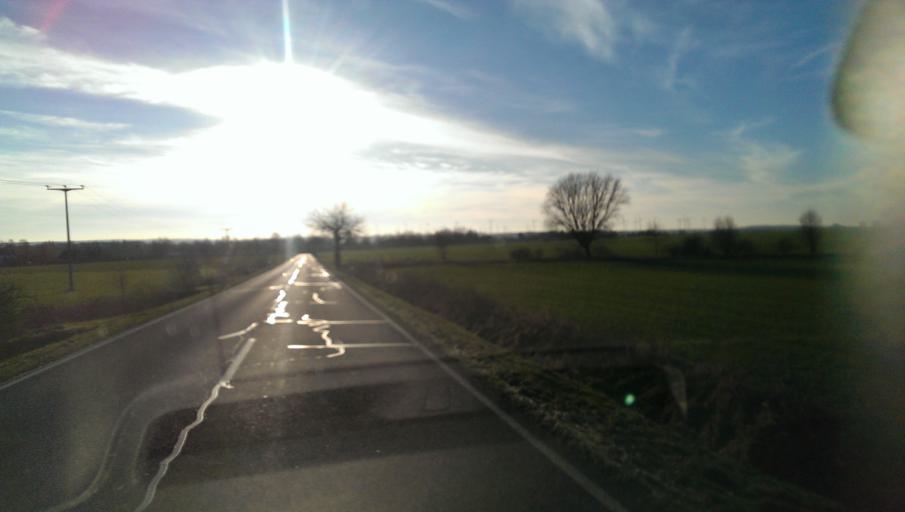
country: DE
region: Saxony-Anhalt
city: Eilsleben
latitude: 52.1563
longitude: 11.2250
